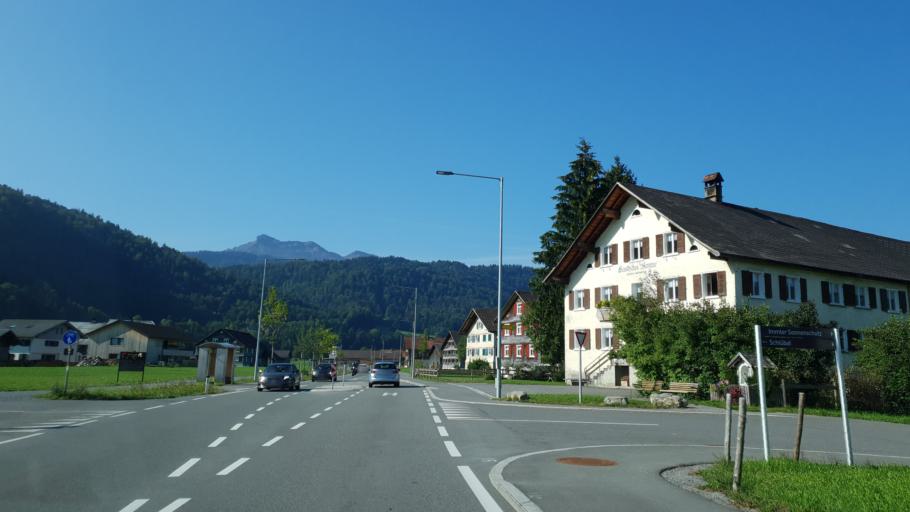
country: AT
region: Vorarlberg
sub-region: Politischer Bezirk Bregenz
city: Andelsbuch
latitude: 47.4093
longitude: 9.8903
